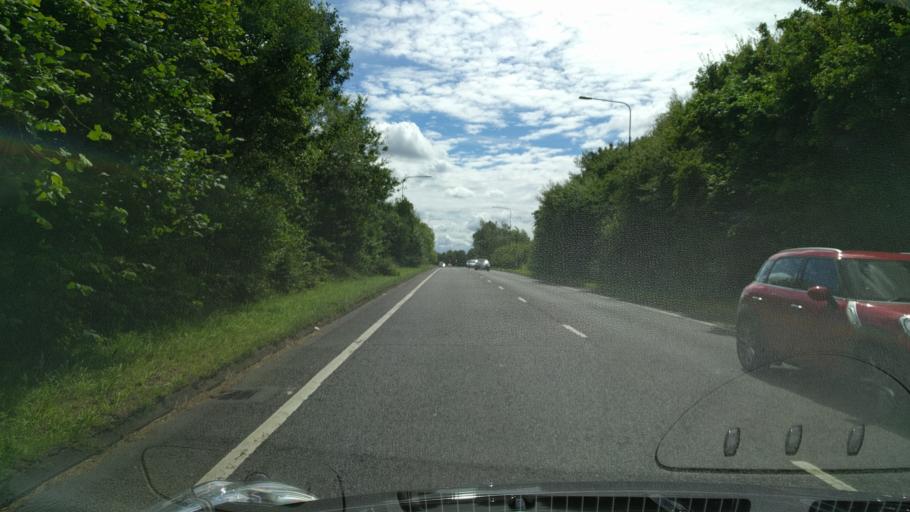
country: GB
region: England
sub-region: Borough of Wigan
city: Leigh
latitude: 53.4750
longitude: -2.5358
